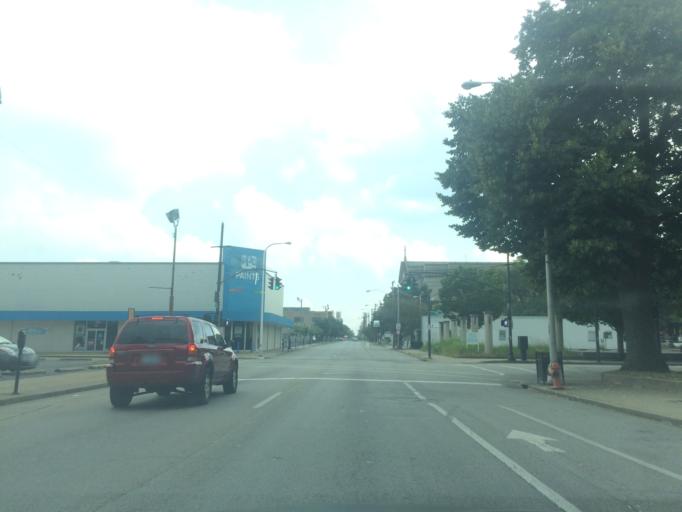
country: US
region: Kentucky
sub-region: Jefferson County
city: Louisville
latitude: 38.2445
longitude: -85.7570
